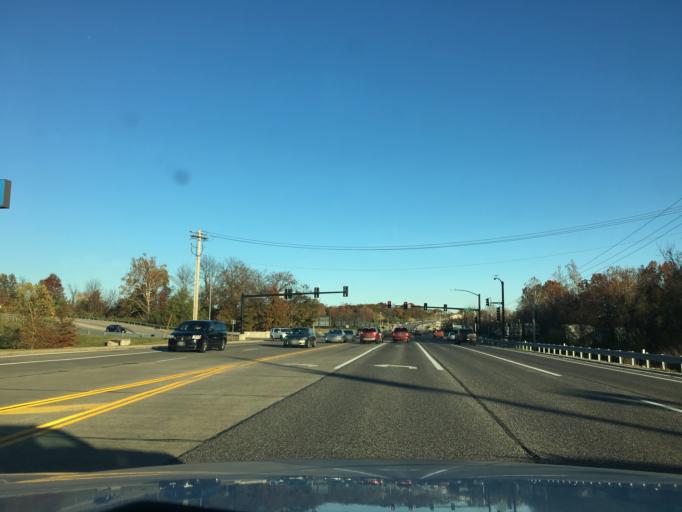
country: US
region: Missouri
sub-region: Franklin County
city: Washington
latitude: 38.5390
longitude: -90.9945
